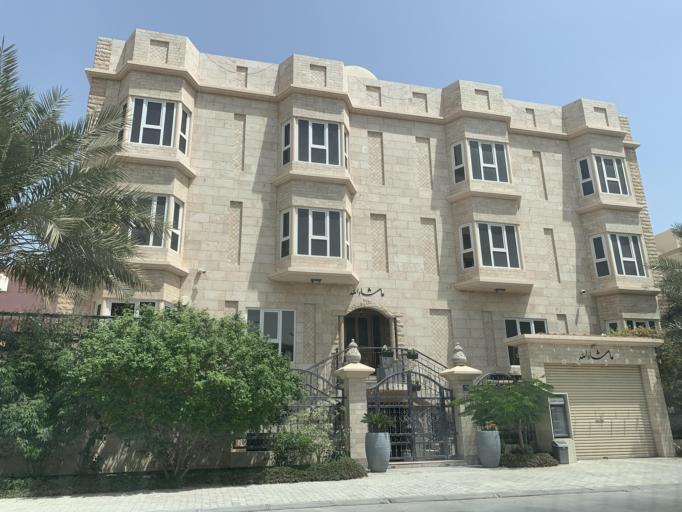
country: BH
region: Northern
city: Sitrah
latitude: 26.1585
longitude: 50.5840
